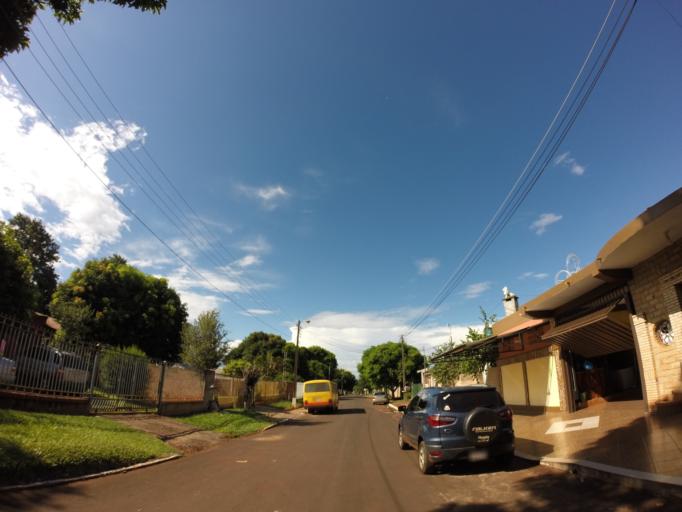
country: PY
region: Alto Parana
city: Ciudad del Este
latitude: -25.4038
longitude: -54.6247
